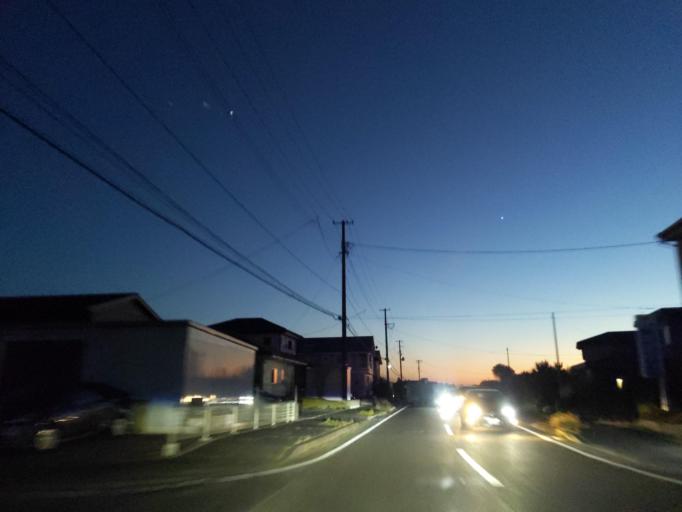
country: JP
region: Fukushima
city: Sukagawa
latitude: 37.3168
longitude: 140.3894
